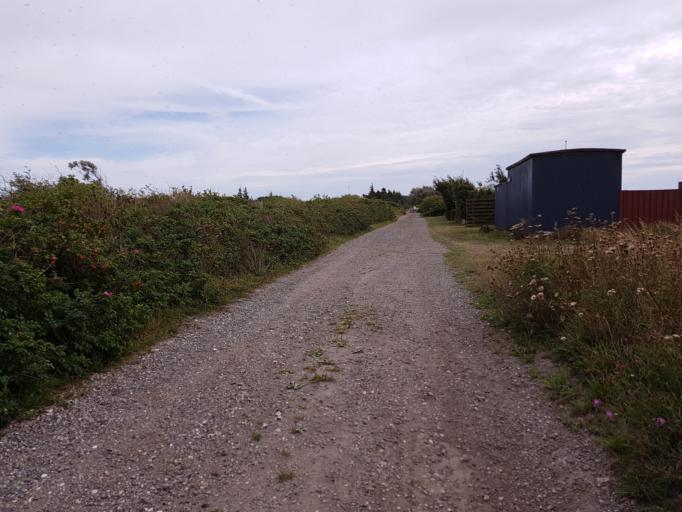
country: DK
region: Zealand
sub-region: Guldborgsund Kommune
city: Nykobing Falster
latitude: 54.5873
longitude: 11.9225
